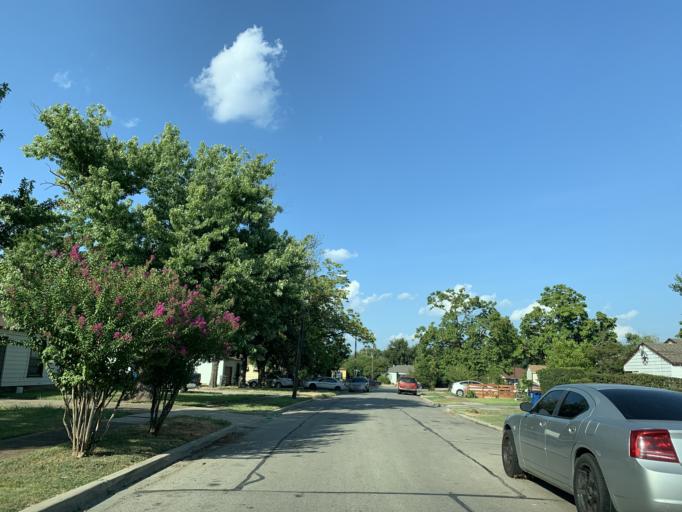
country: US
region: Texas
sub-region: Dallas County
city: Hutchins
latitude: 32.6992
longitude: -96.7774
